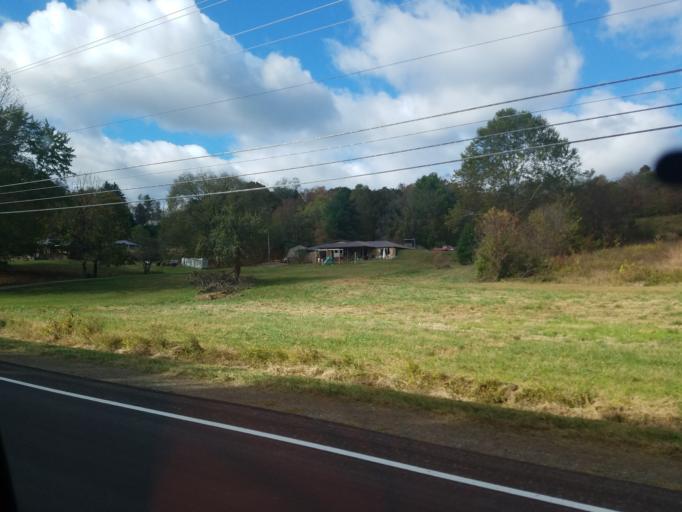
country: US
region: Ohio
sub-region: Vinton County
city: McArthur
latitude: 39.2313
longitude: -82.4806
